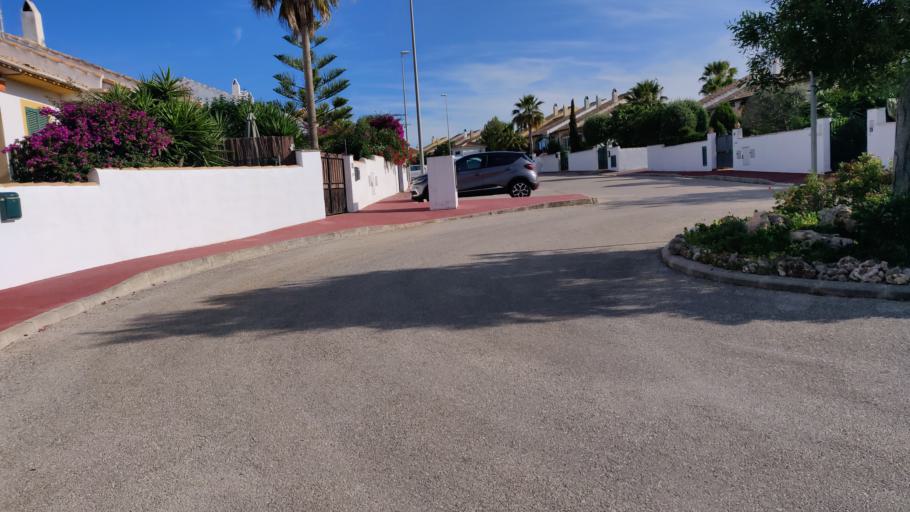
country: ES
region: Balearic Islands
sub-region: Illes Balears
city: Felanitx
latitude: 39.4532
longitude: 3.2603
